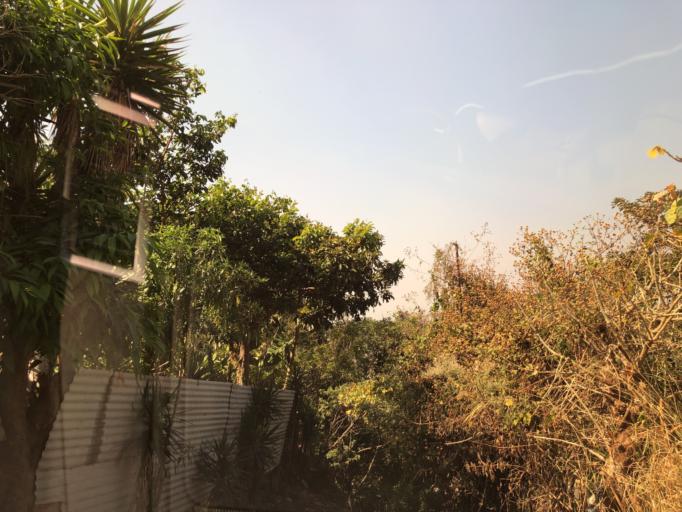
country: GT
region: Guatemala
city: Santa Catarina Pinula
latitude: 14.5369
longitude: -90.5101
